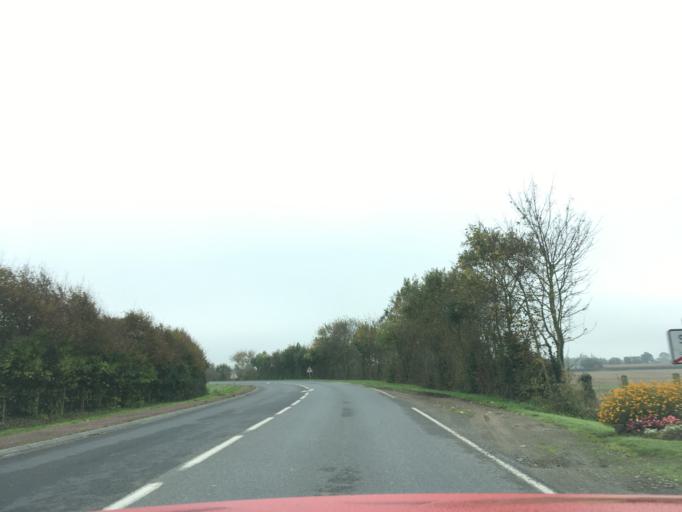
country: FR
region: Lower Normandy
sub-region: Departement de la Manche
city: Saint-Pair-sur-Mer
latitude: 48.8137
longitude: -1.5547
